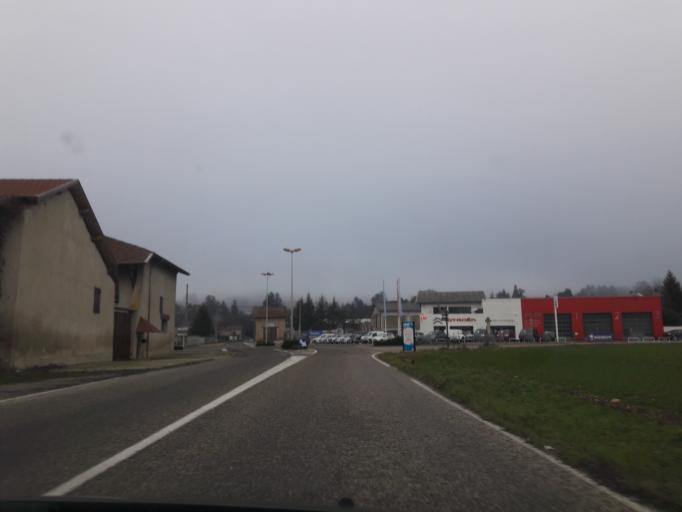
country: FR
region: Rhone-Alpes
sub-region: Departement de l'Isere
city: La Cote-Saint-Andre
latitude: 45.3872
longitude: 5.2722
